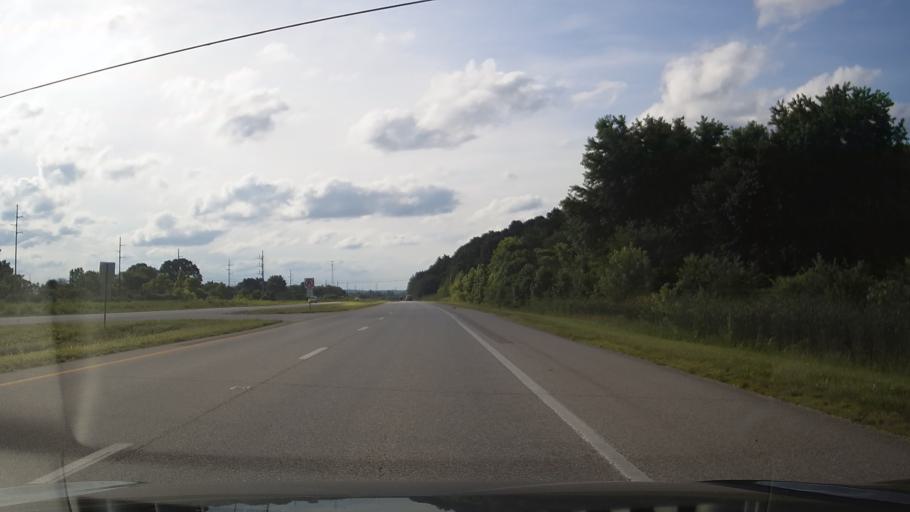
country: US
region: Ohio
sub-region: Scioto County
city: Franklin Furnace
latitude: 38.6230
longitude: -82.8359
